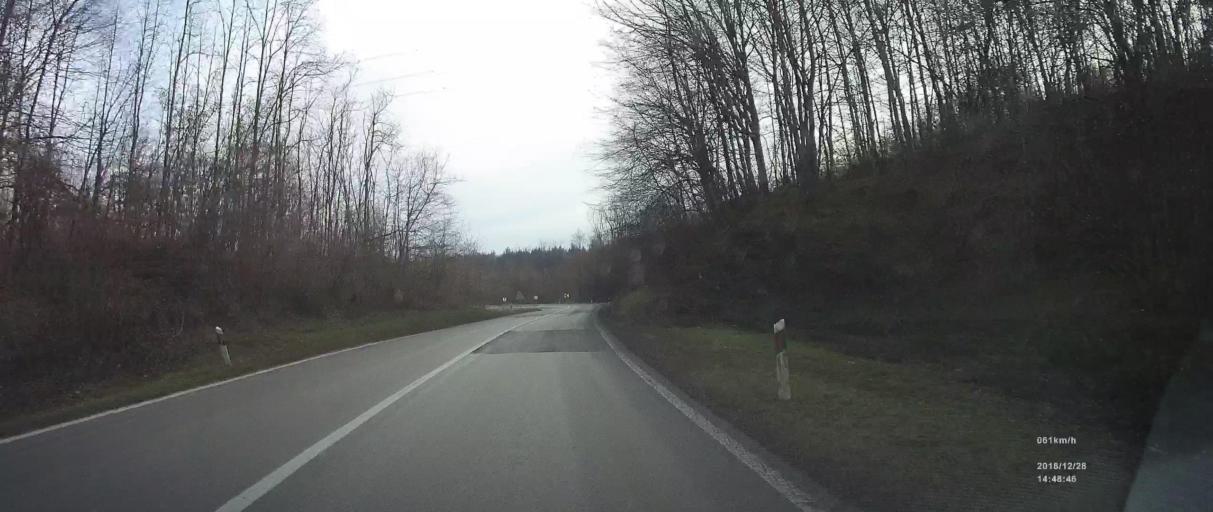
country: HR
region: Karlovacka
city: Ozalj
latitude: 45.4452
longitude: 15.3455
